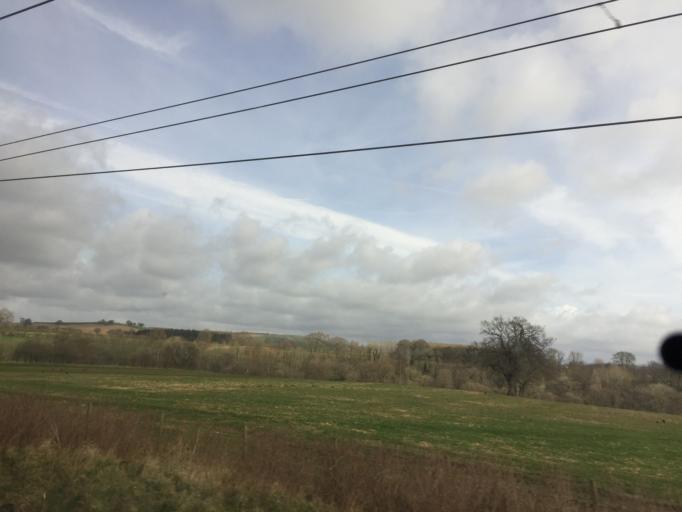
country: GB
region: England
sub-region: Cumbria
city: Penrith
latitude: 54.7496
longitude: -2.8116
